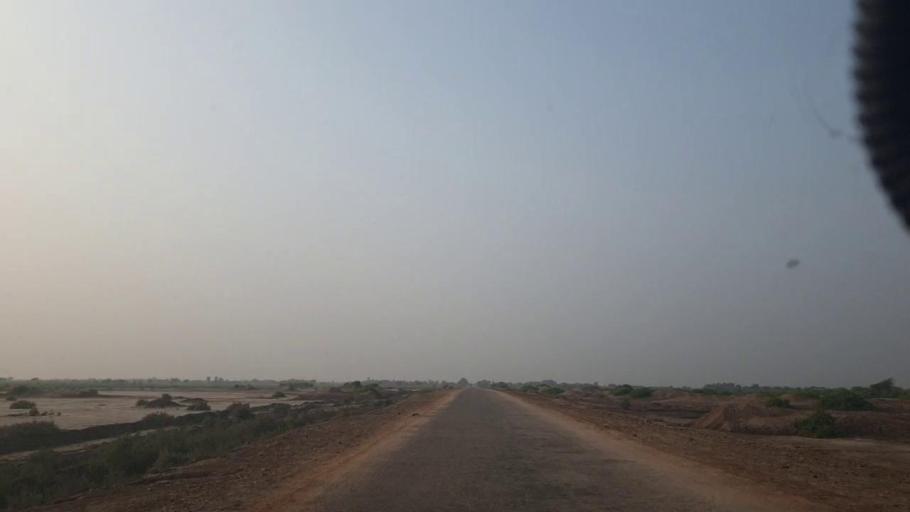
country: PK
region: Sindh
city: Bulri
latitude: 24.8562
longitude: 68.4015
